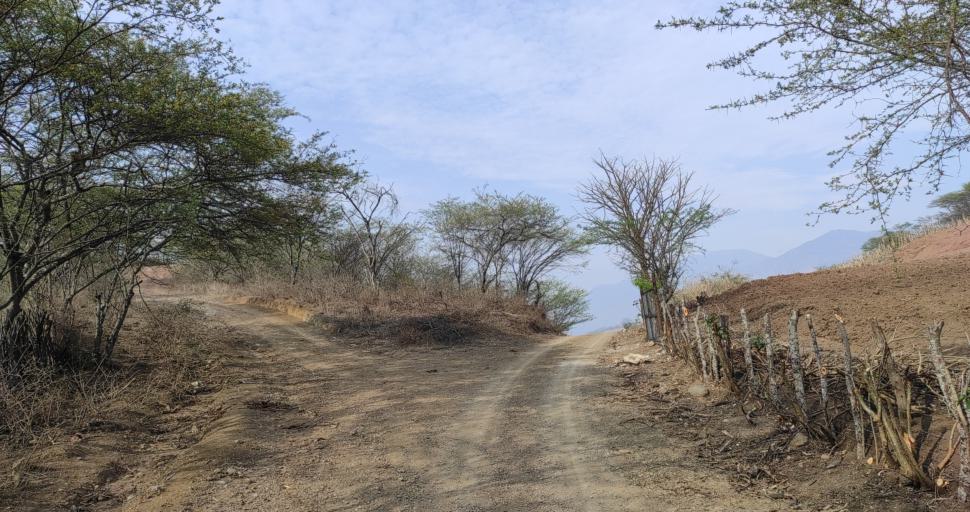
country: EC
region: Loja
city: Catacocha
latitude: -4.0099
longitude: -79.7016
